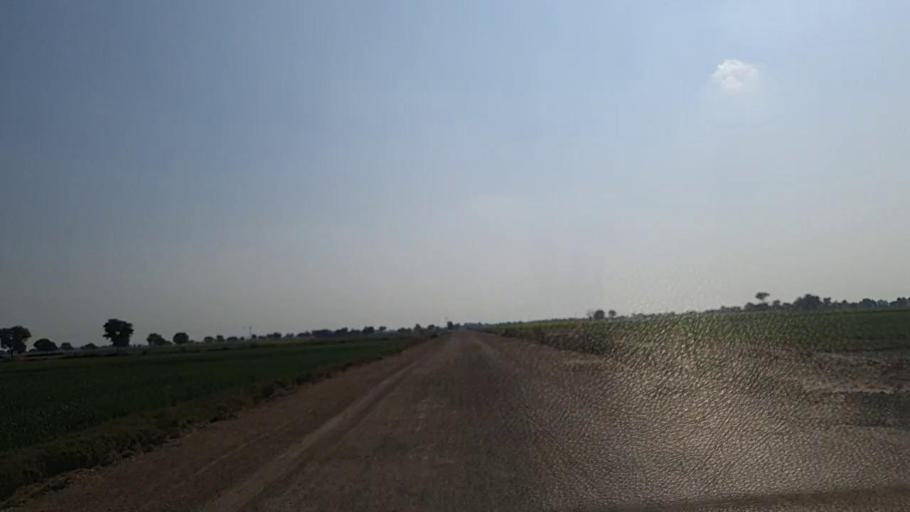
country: PK
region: Sindh
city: Jam Sahib
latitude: 26.2557
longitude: 68.5669
